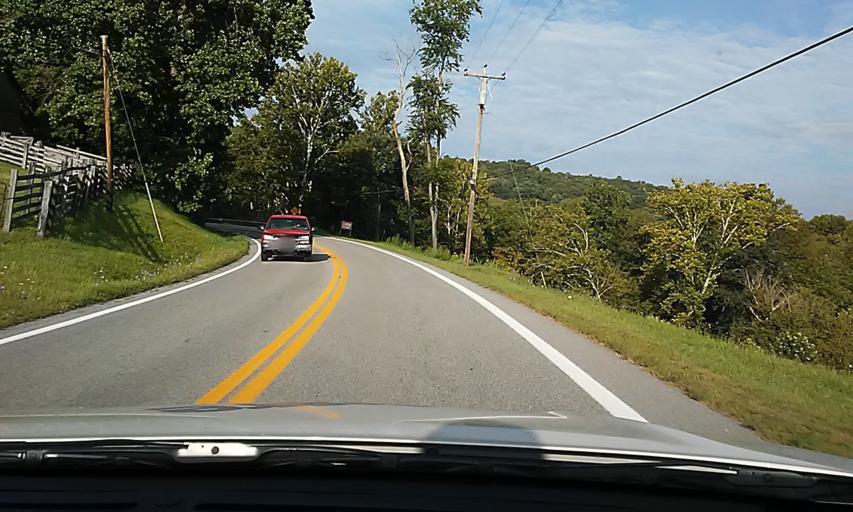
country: US
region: Pennsylvania
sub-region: Greene County
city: Waynesburg
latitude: 39.7210
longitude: -80.2375
